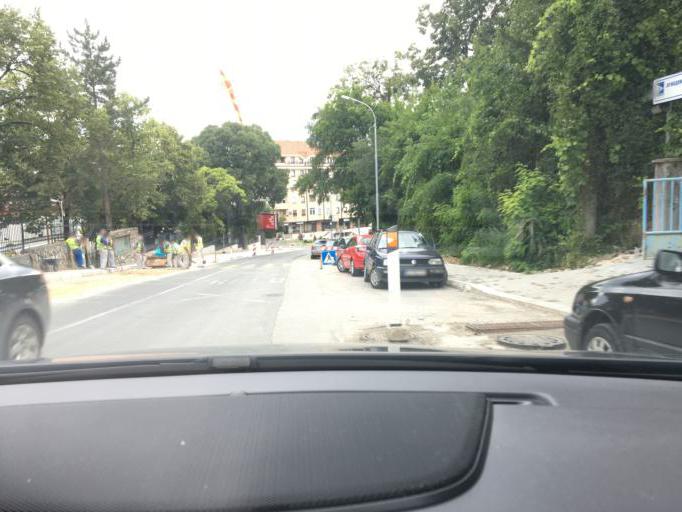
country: MK
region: Karpos
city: Skopje
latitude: 41.9872
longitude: 21.4176
